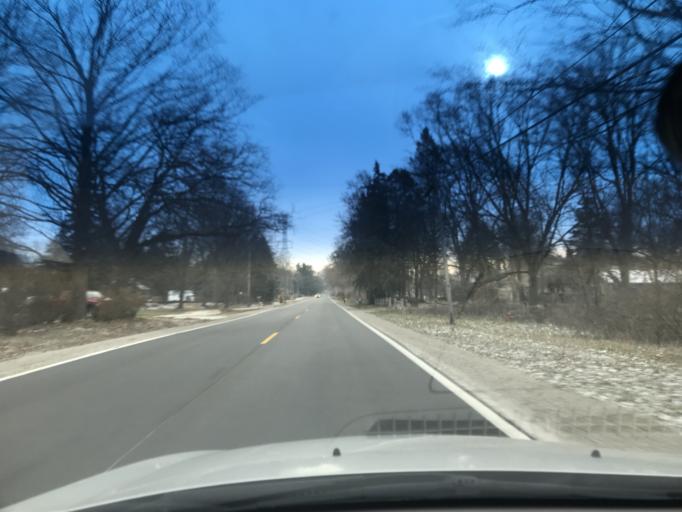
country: US
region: Michigan
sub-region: Macomb County
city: Shelby
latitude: 42.6631
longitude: -83.0586
